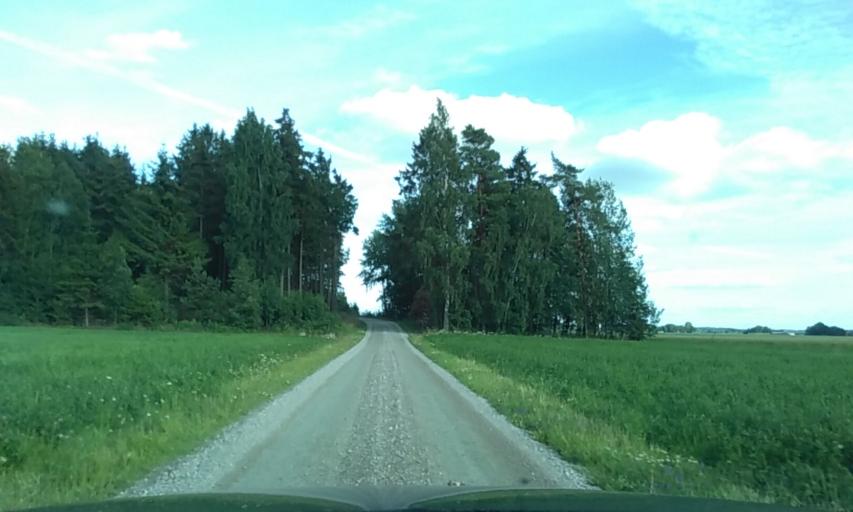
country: SE
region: Vaestra Goetaland
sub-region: Grastorps Kommun
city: Graestorp
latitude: 58.3777
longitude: 12.7999
